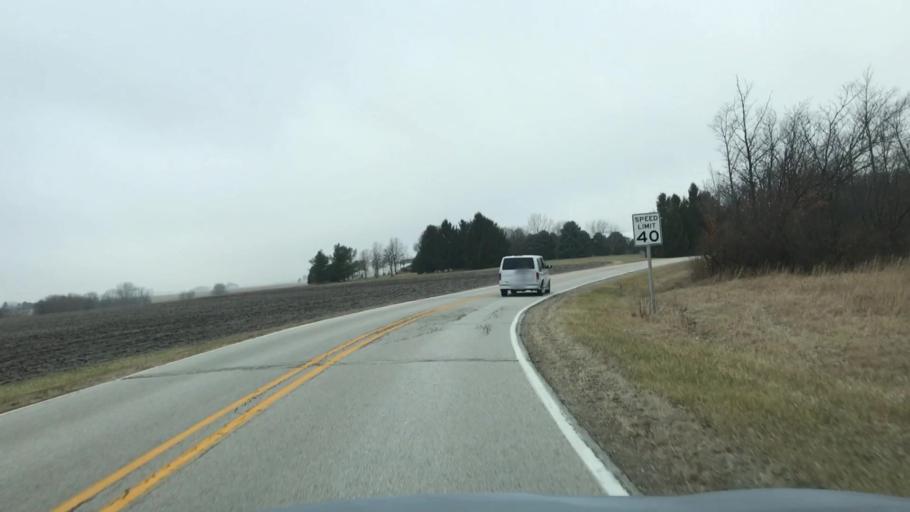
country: US
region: Illinois
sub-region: McLean County
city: Hudson
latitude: 40.6263
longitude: -88.9319
